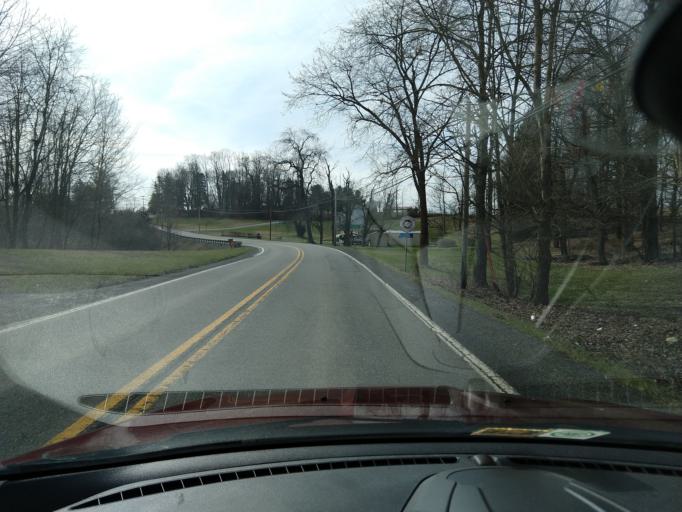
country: US
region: West Virginia
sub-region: Greenbrier County
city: Lewisburg
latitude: 37.8687
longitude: -80.4106
